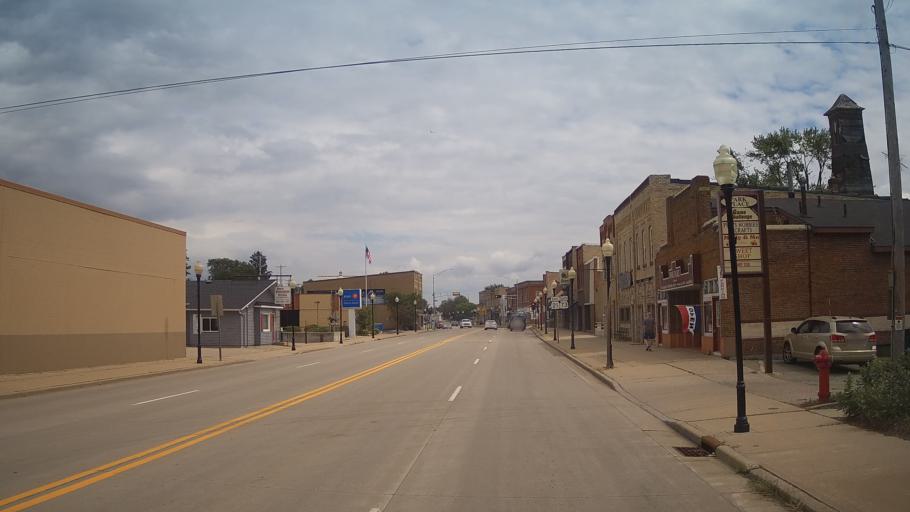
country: US
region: Wisconsin
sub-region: Waushara County
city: Wautoma
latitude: 44.0757
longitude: -89.2929
